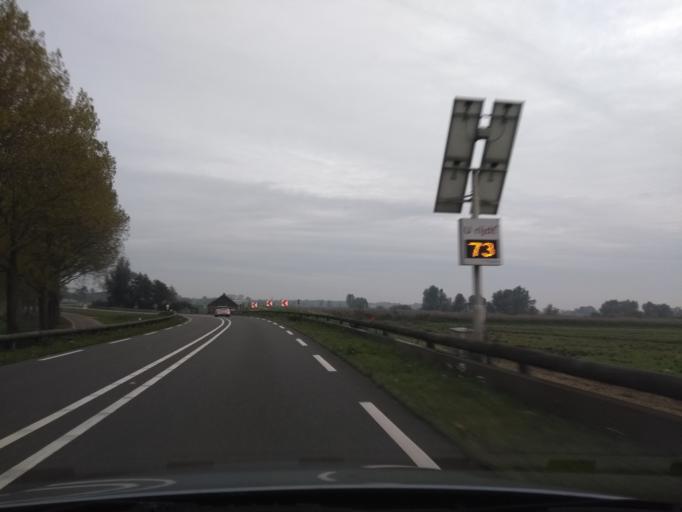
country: NL
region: Overijssel
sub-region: Gemeente Zwartewaterland
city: Hasselt
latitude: 52.6129
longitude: 6.0921
